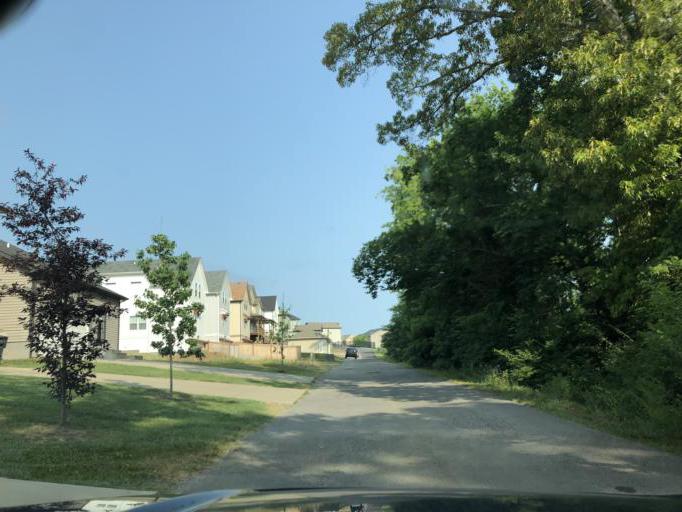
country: US
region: Tennessee
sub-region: Rutherford County
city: La Vergne
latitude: 36.0487
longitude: -86.6410
